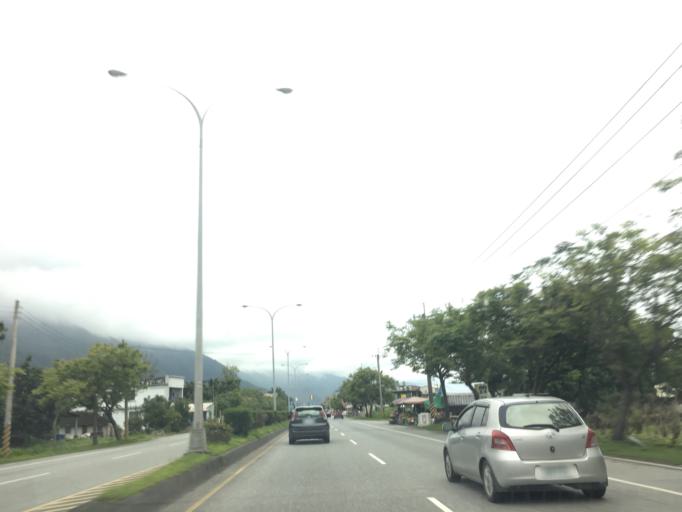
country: TW
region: Taiwan
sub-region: Hualien
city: Hualian
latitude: 24.0454
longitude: 121.6042
